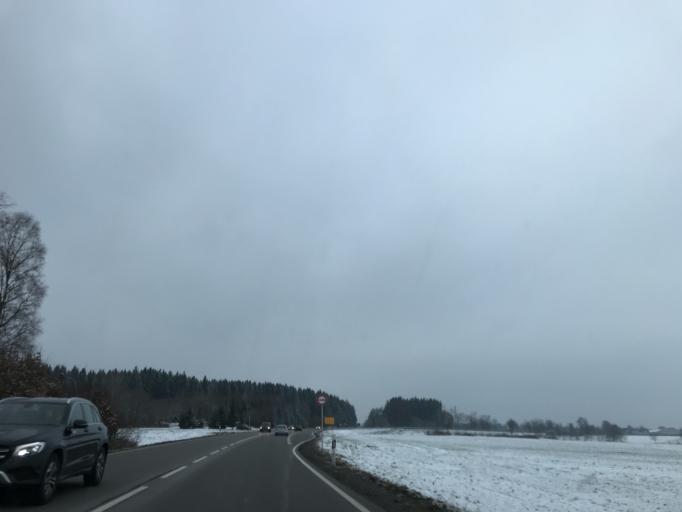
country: DE
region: Baden-Wuerttemberg
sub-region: Freiburg Region
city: Monchweiler
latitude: 48.0879
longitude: 8.4344
